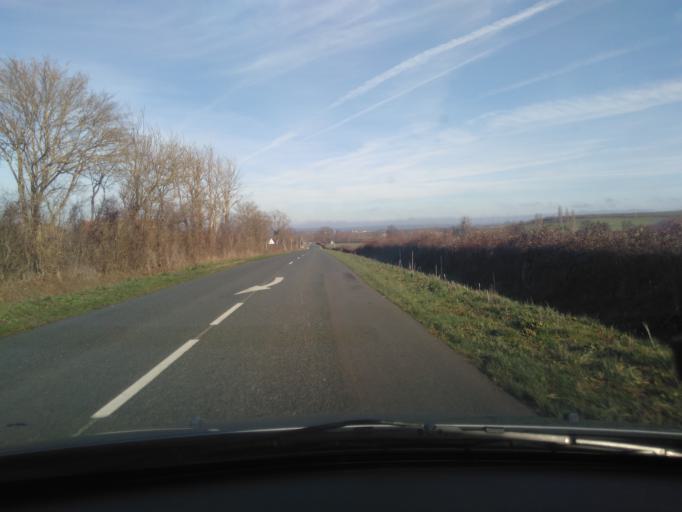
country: FR
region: Centre
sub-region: Departement du Cher
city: Orval
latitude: 46.6817
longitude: 2.4628
